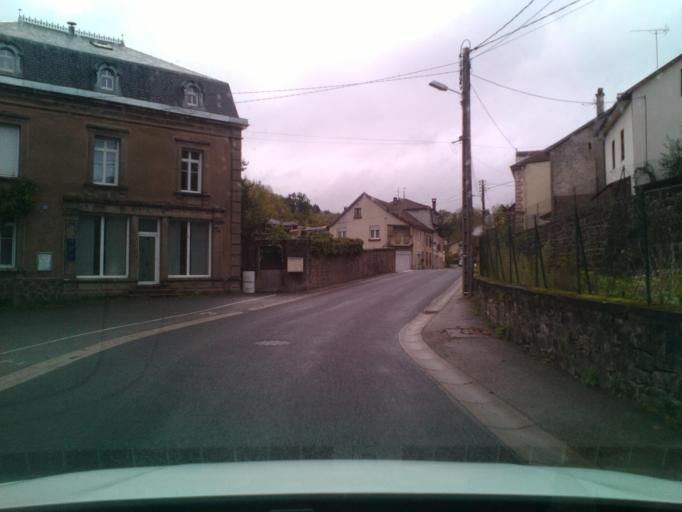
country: FR
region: Lorraine
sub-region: Departement des Vosges
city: Moyenmoutier
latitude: 48.3779
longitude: 6.9142
